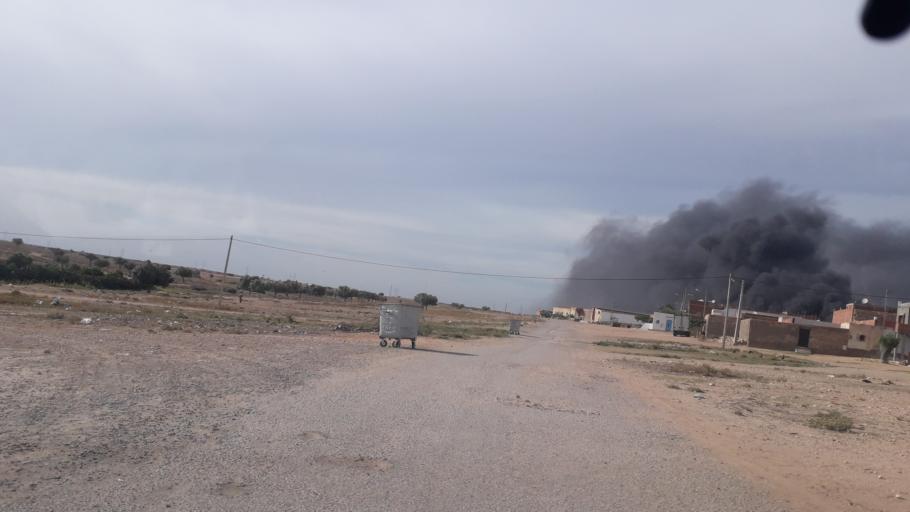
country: TN
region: Safaqis
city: Al Qarmadah
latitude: 34.8854
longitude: 10.7579
